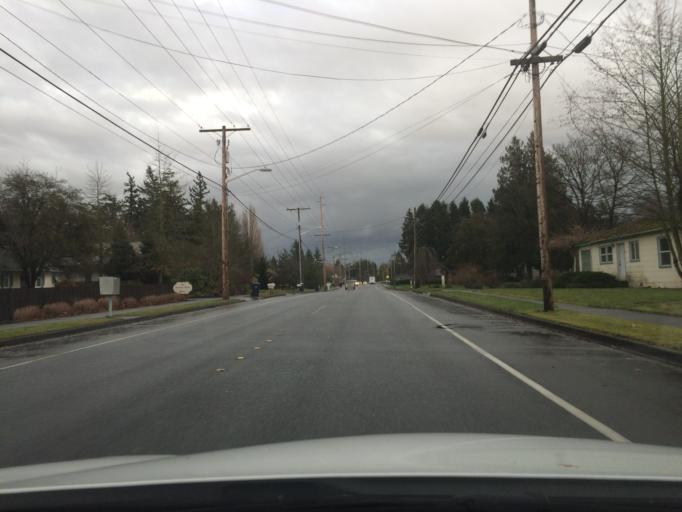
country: US
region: Washington
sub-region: Whatcom County
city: Lynden
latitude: 48.9466
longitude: -122.4686
